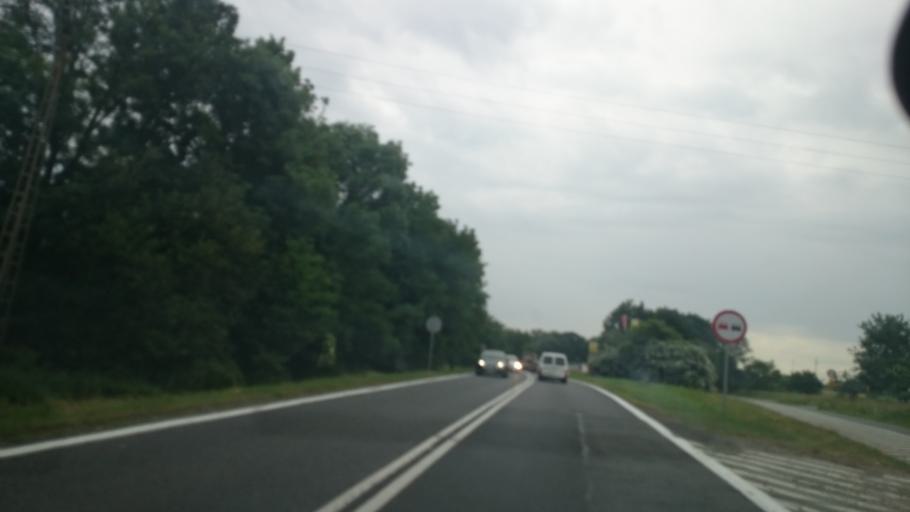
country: PL
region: Lower Silesian Voivodeship
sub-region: Powiat dzierzoniowski
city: Niemcza
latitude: 50.7360
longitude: 16.8376
